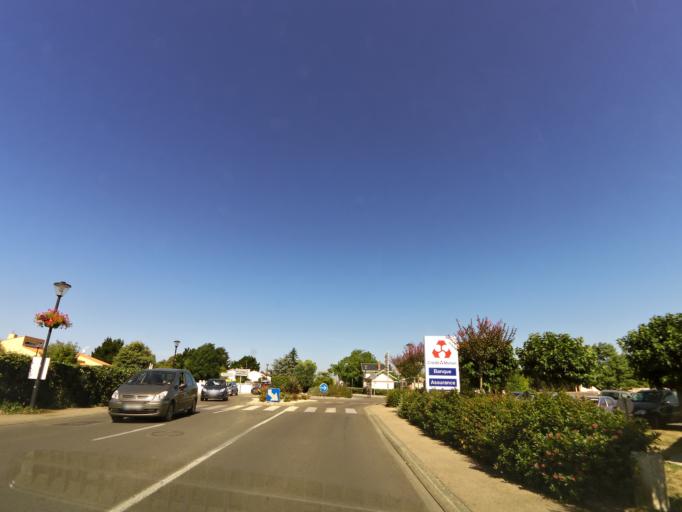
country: FR
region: Pays de la Loire
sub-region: Departement de la Vendee
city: Jard-sur-Mer
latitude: 46.4161
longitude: -1.5485
